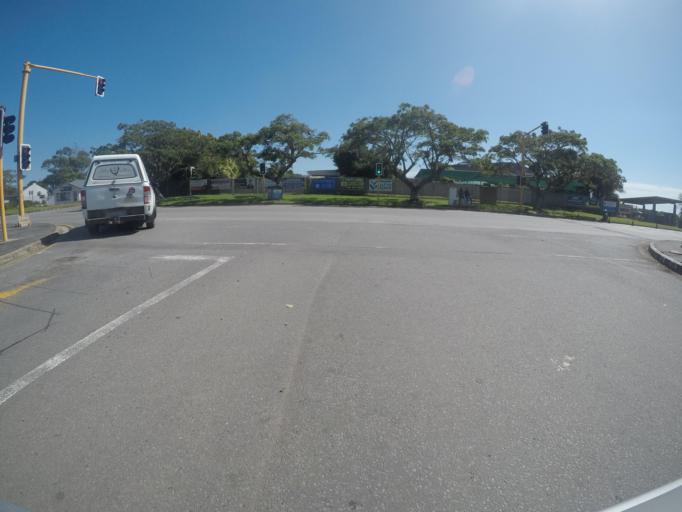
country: ZA
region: Eastern Cape
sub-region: Buffalo City Metropolitan Municipality
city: East London
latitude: -32.9378
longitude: 28.0078
